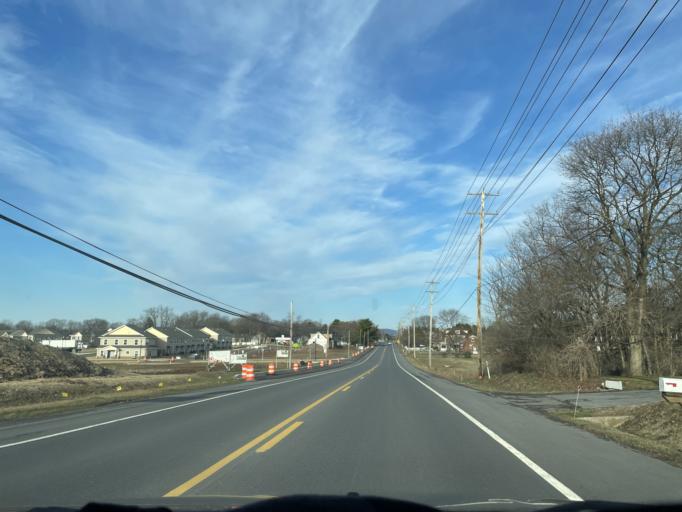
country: US
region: Maryland
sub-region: Washington County
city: Halfway
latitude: 39.6494
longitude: -77.7613
